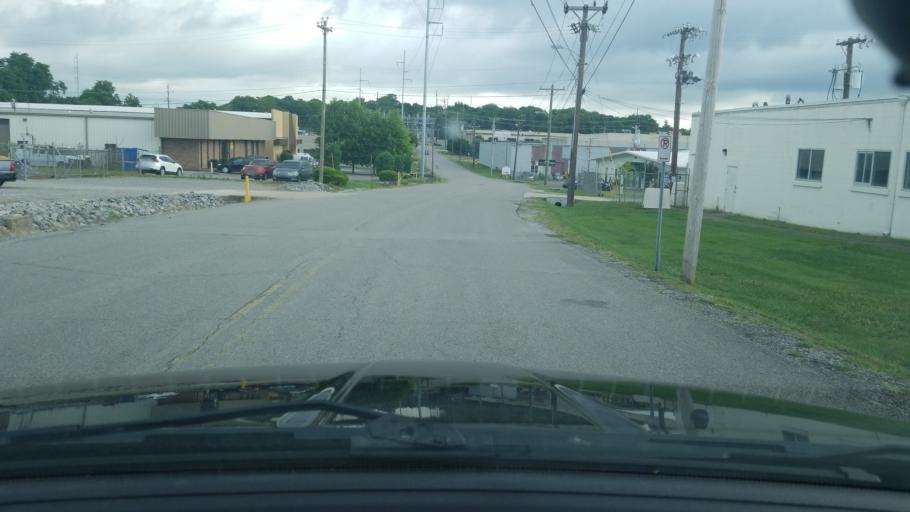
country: US
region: Tennessee
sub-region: Davidson County
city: Oak Hill
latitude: 36.0932
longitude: -86.7469
